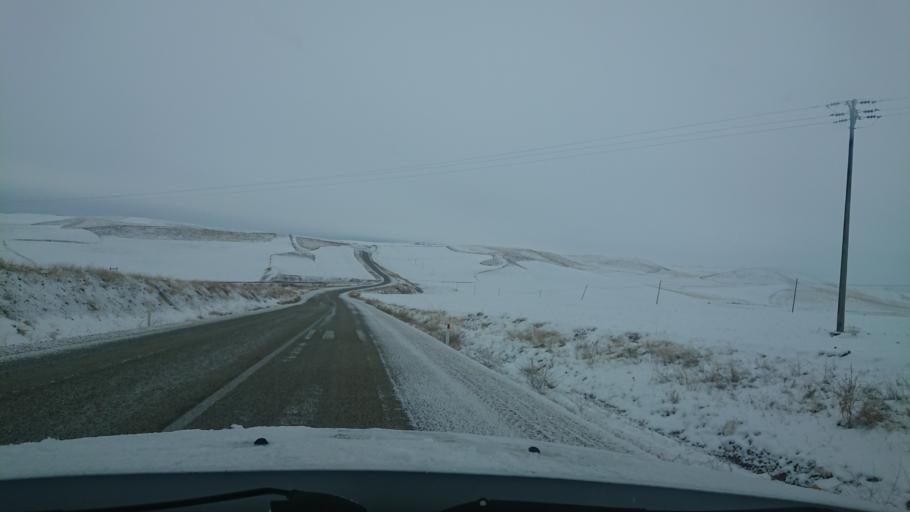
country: TR
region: Aksaray
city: Agacoren
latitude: 38.7846
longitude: 33.8712
